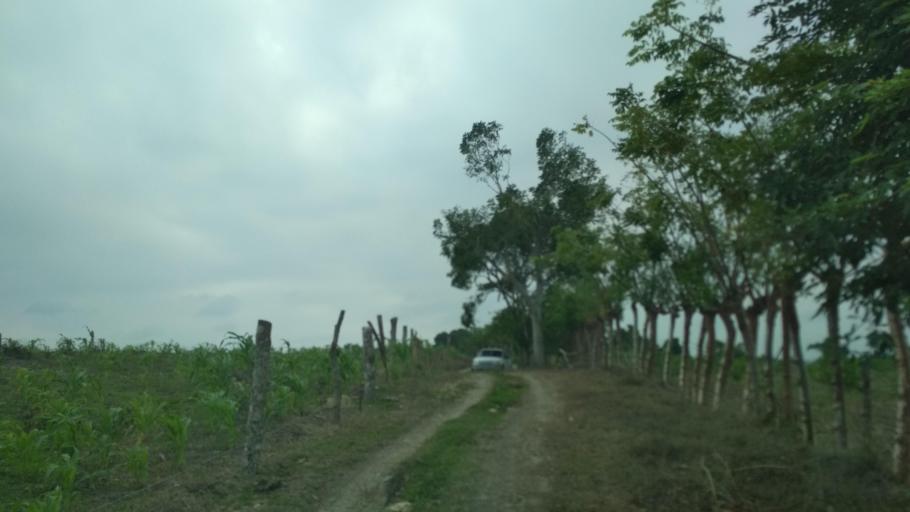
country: MM
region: Kayah
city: Loikaw
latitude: 20.2078
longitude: 97.3267
